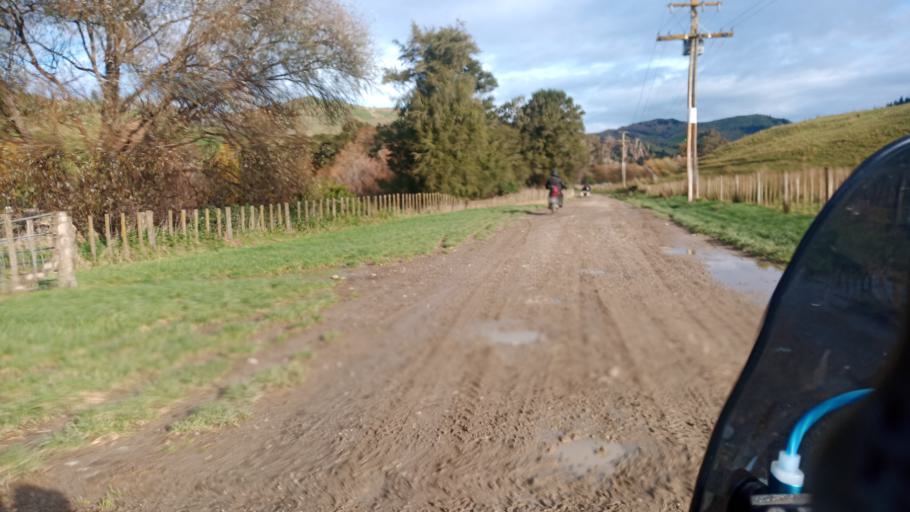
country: NZ
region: Gisborne
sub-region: Gisborne District
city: Gisborne
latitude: -38.3500
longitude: 177.9393
